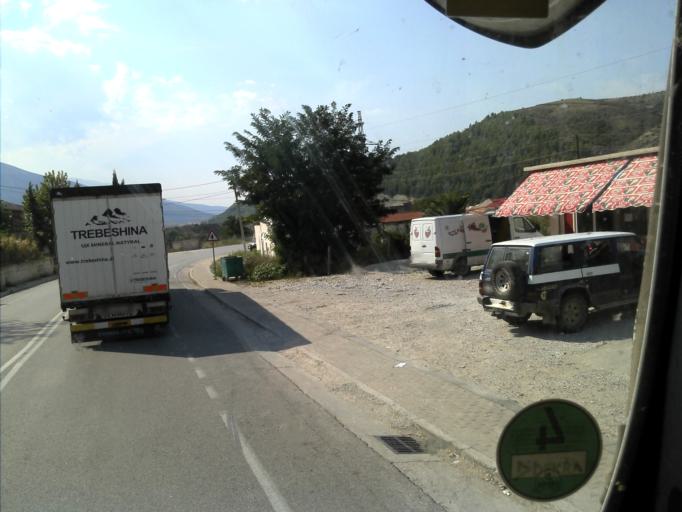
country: AL
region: Gjirokaster
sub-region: Rrethi i Tepelenes
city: Memaliaj
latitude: 40.3495
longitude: 19.9756
